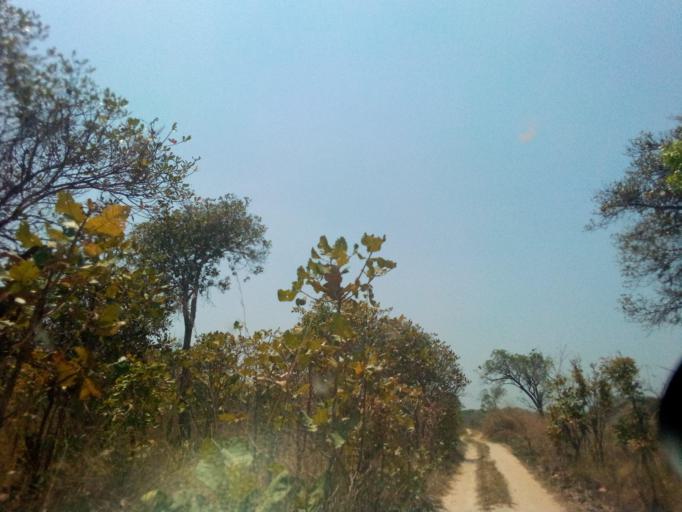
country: ZM
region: Copperbelt
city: Kataba
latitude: -12.2486
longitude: 30.3932
